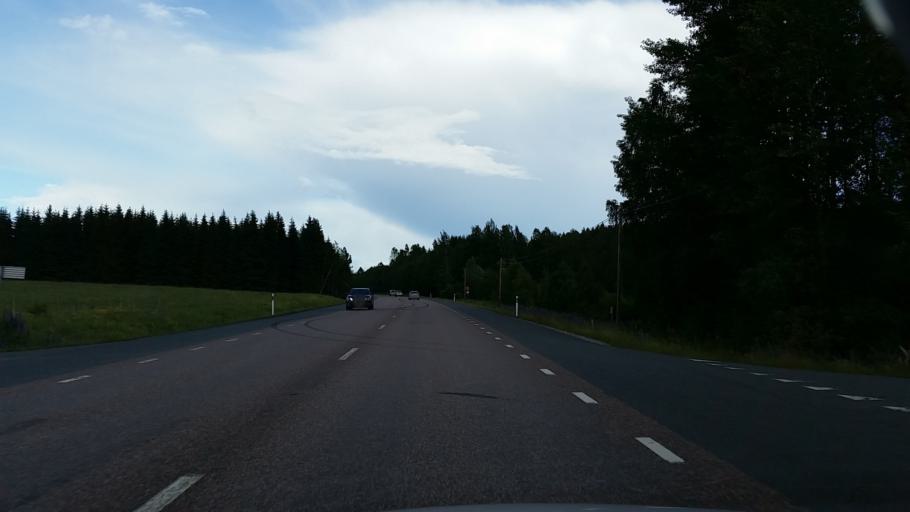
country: SE
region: Vaestmanland
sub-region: Fagersta Kommun
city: Fagersta
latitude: 59.9656
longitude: 15.7353
